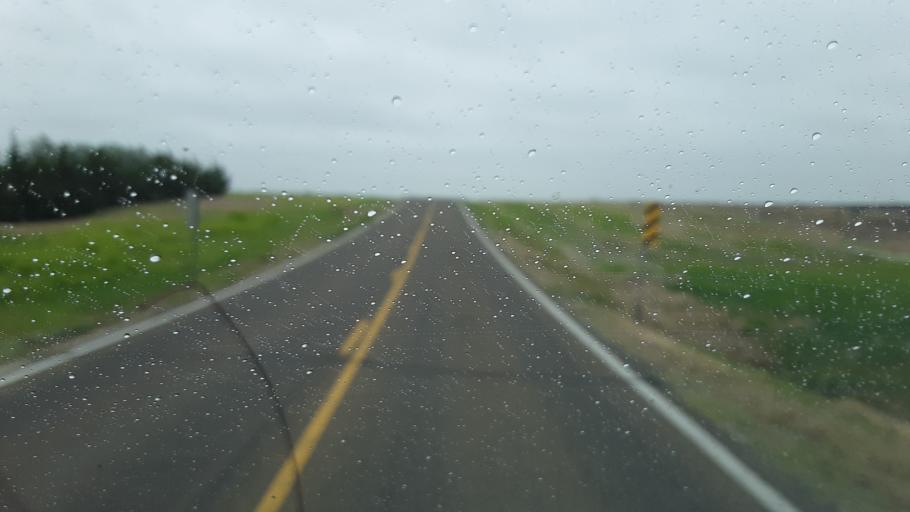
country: US
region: Kansas
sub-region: Logan County
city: Oakley
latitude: 39.1131
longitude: -100.9512
